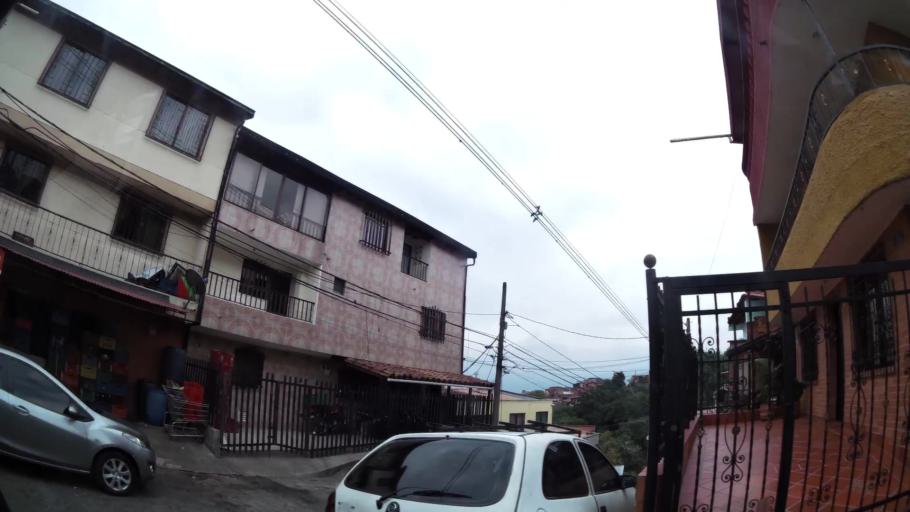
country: CO
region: Antioquia
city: Medellin
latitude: 6.2846
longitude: -75.5881
